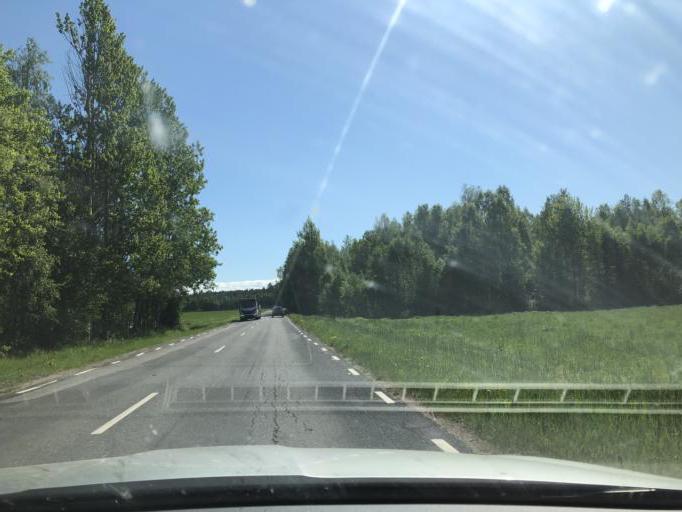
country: SE
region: Norrbotten
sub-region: Lulea Kommun
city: Gammelstad
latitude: 65.6603
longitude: 21.9850
